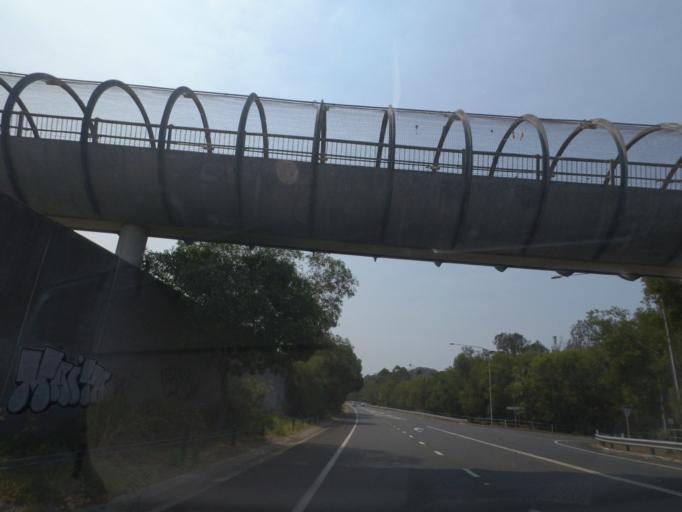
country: AU
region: New South Wales
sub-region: Byron Shire
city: Brunswick Heads
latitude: -28.5031
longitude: 153.5299
